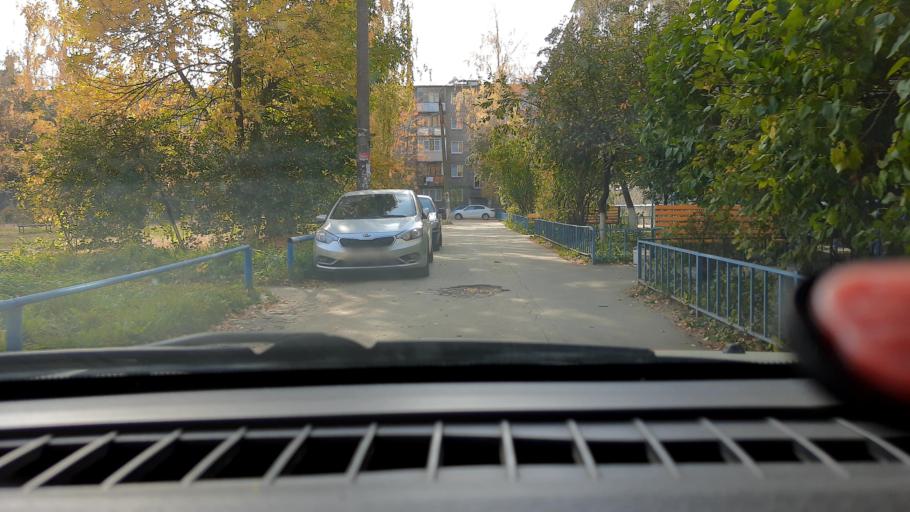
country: RU
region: Nizjnij Novgorod
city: Nizhniy Novgorod
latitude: 56.2803
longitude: 43.9171
